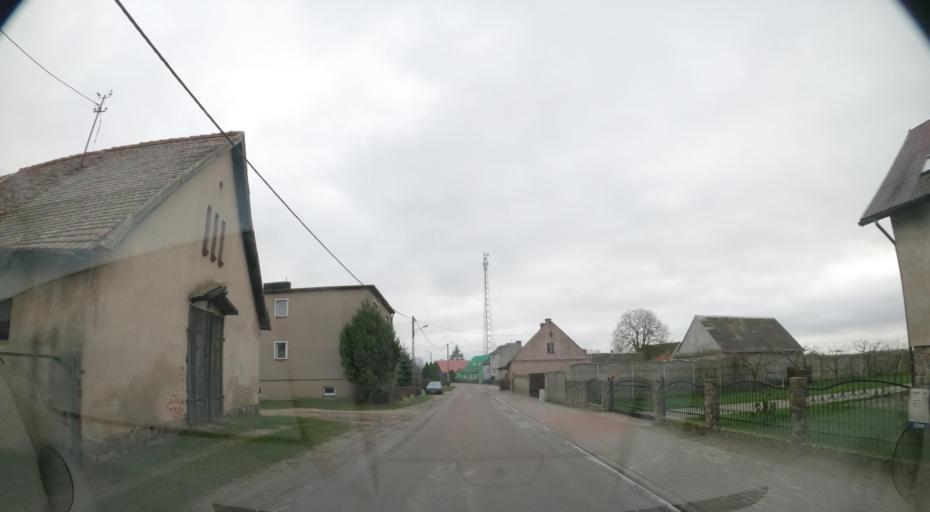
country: PL
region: Greater Poland Voivodeship
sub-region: Powiat pilski
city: Wysoka
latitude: 53.2562
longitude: 17.1230
